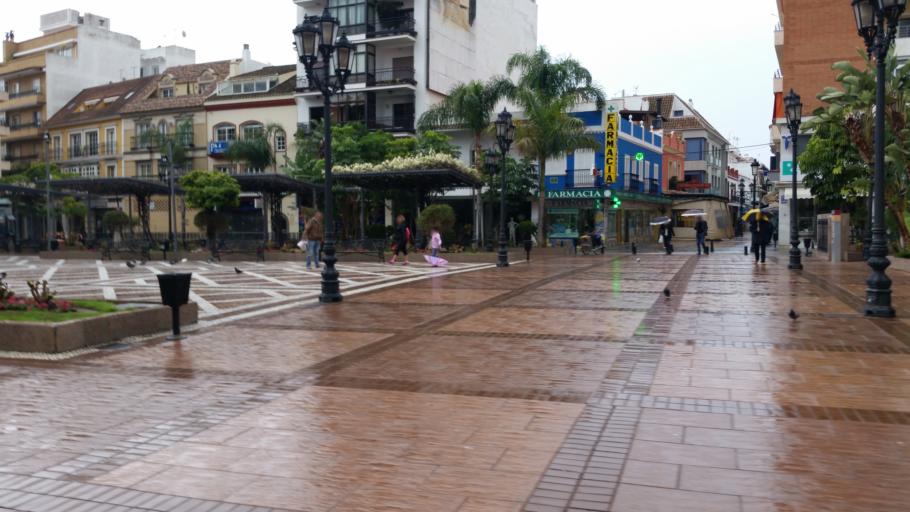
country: ES
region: Andalusia
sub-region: Provincia de Malaga
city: Fuengirola
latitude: 36.5391
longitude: -4.6235
